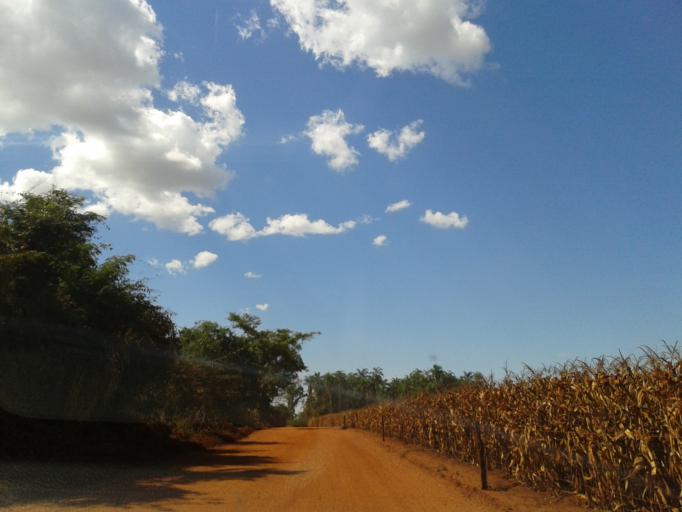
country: BR
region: Minas Gerais
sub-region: Capinopolis
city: Capinopolis
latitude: -18.6186
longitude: -49.4761
